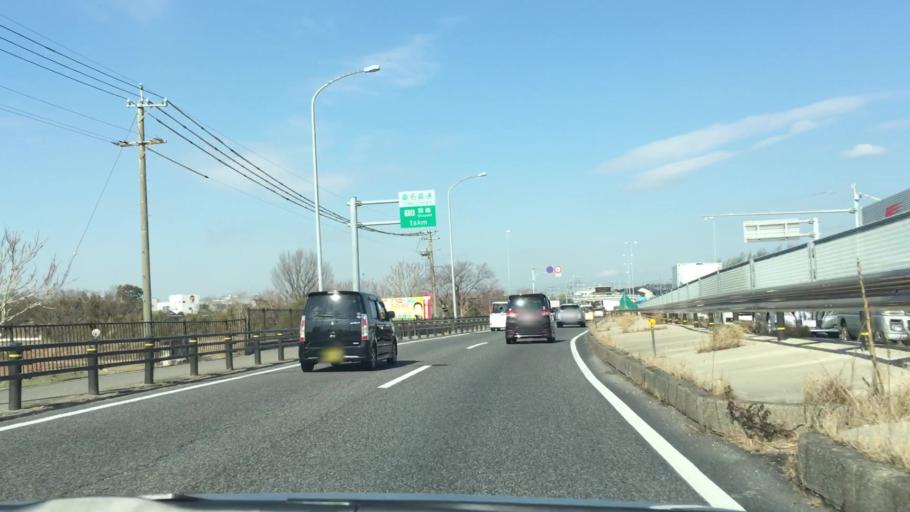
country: JP
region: Aichi
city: Okazaki
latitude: 34.9323
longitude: 137.1966
